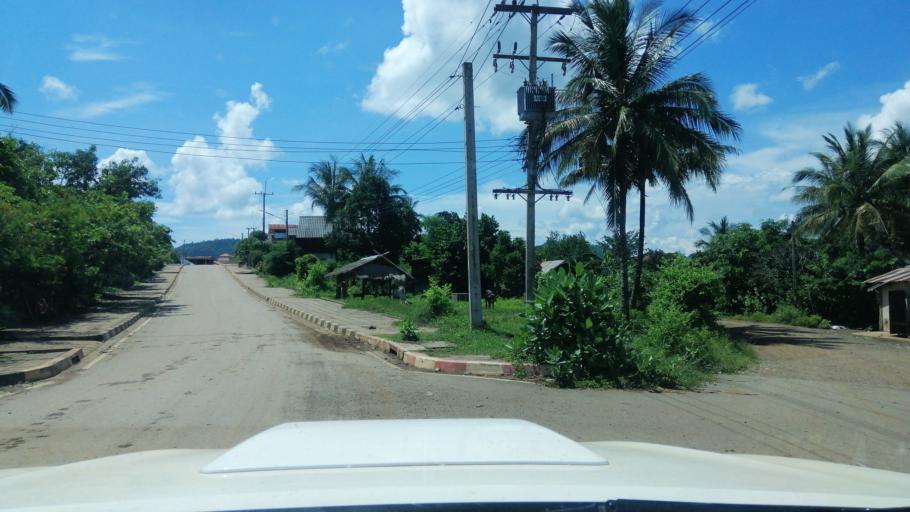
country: TH
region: Uttaradit
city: Ban Khok
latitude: 18.1360
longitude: 101.2721
